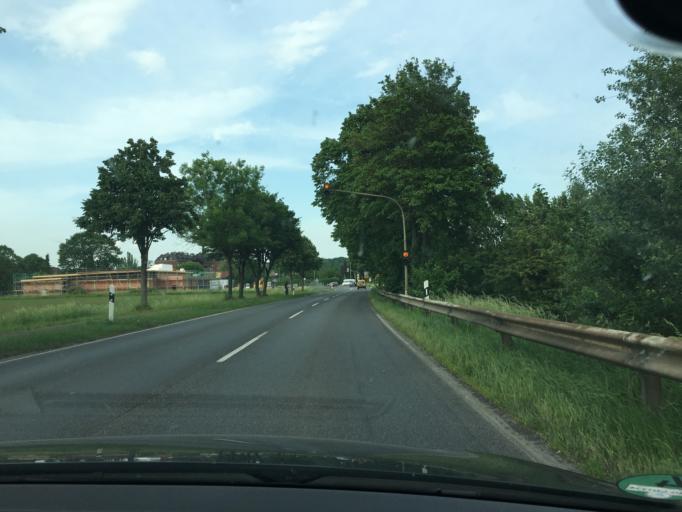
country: DE
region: North Rhine-Westphalia
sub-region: Regierungsbezirk Koln
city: Kreuzau
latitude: 50.7607
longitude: 6.4921
